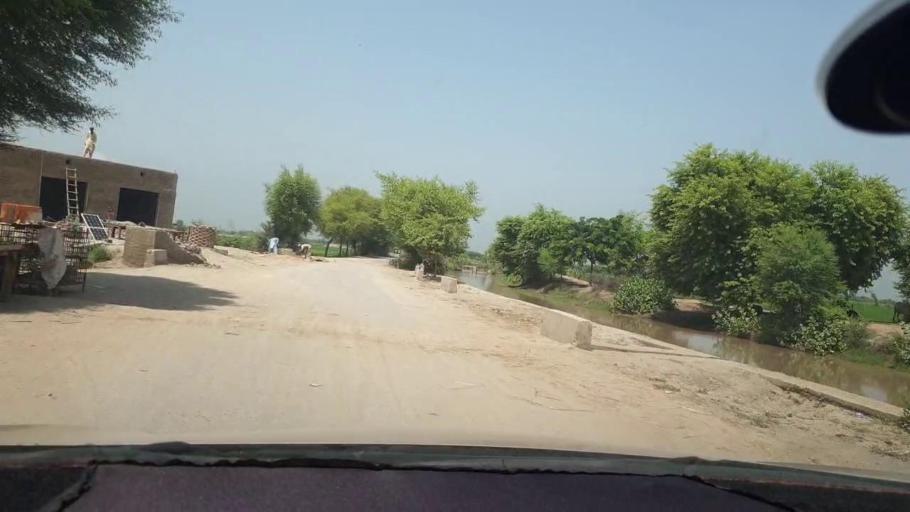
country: PK
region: Sindh
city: Kambar
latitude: 27.6372
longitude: 67.9782
